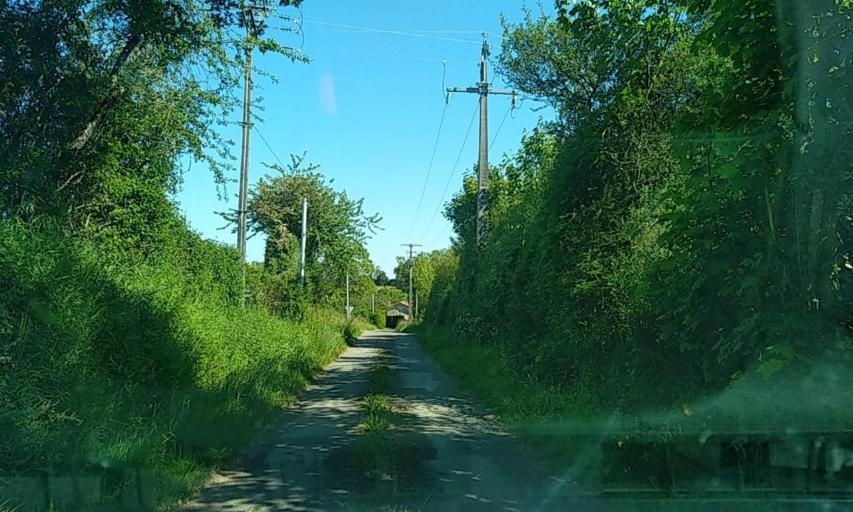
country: FR
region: Poitou-Charentes
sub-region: Departement des Deux-Sevres
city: Boisme
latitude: 46.7870
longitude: -0.4513
